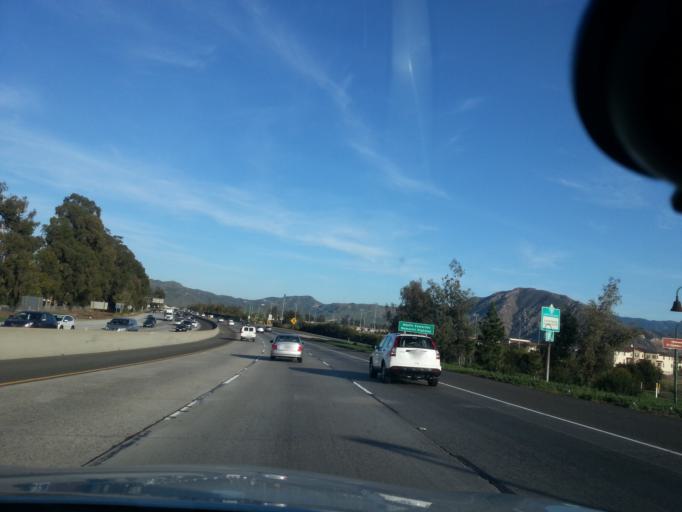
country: US
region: California
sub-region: Ventura County
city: Camarillo
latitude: 34.2159
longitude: -119.0310
